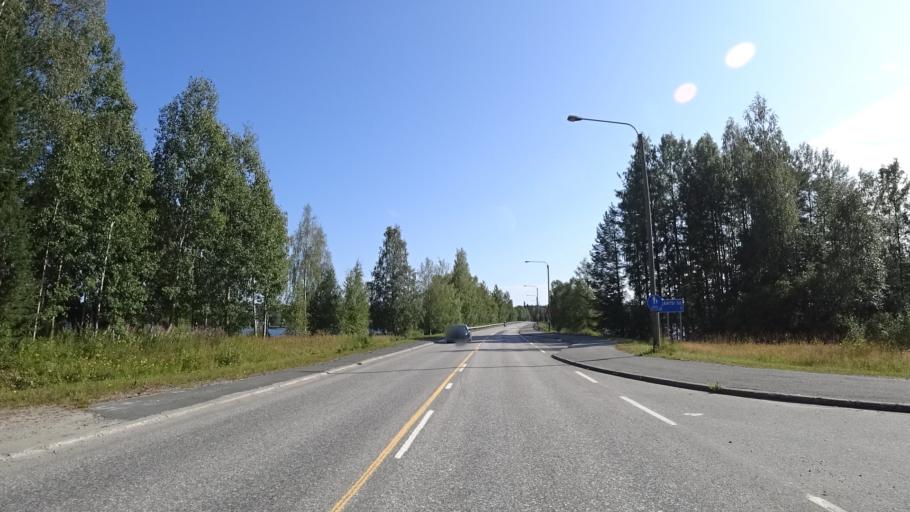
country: FI
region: North Karelia
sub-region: Joensuu
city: Eno
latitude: 62.8071
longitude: 30.1516
